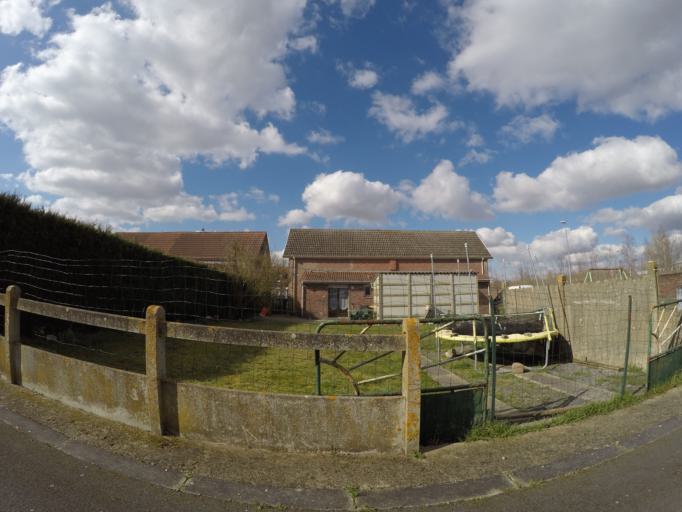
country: FR
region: Nord-Pas-de-Calais
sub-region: Departement du Pas-de-Calais
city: Mazingarbe
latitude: 50.4612
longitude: 2.7259
